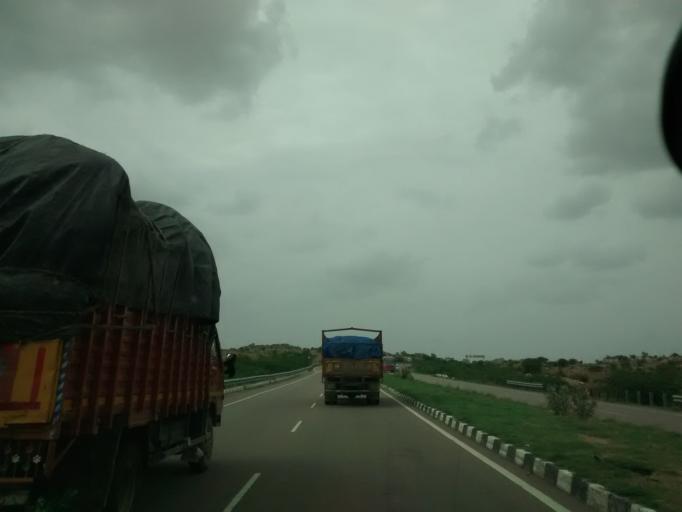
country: IN
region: Andhra Pradesh
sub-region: Kurnool
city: Ramapuram
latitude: 15.1519
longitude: 77.6666
